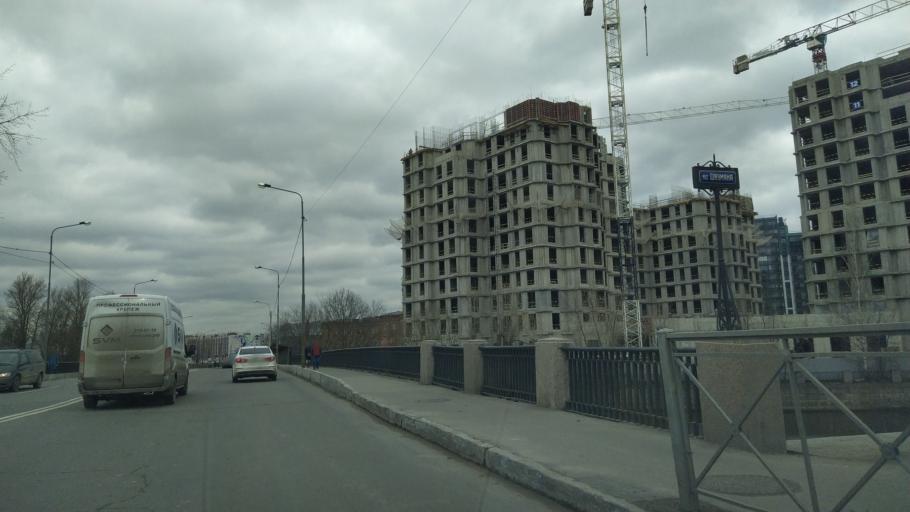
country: RU
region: St.-Petersburg
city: Centralniy
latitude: 59.9335
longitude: 30.4157
